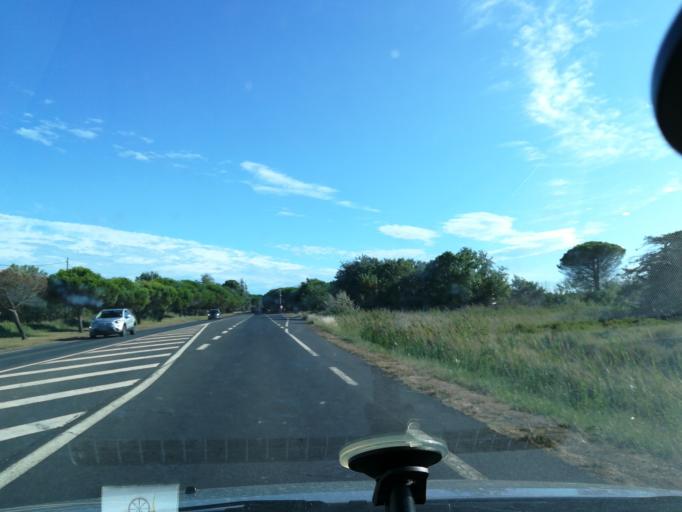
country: FR
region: Languedoc-Roussillon
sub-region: Departement de l'Herault
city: Portiragnes
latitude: 43.2876
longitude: 3.3626
